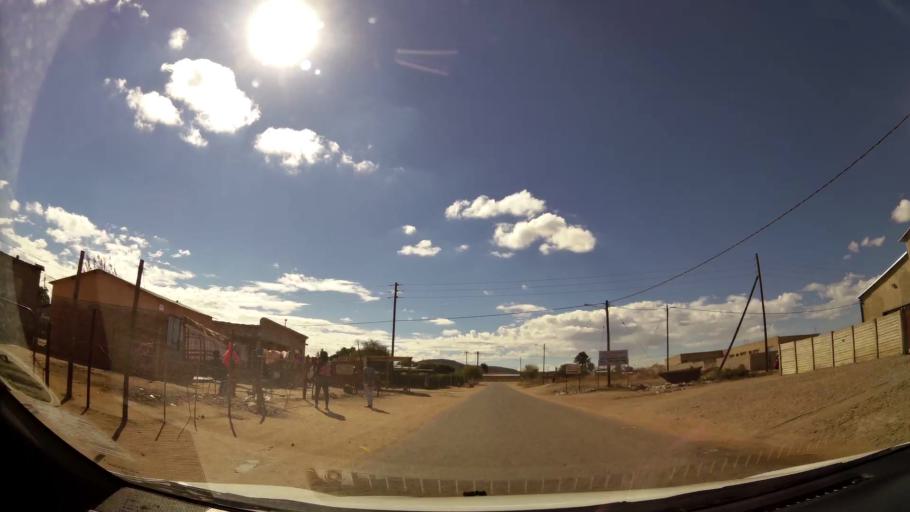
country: ZA
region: Limpopo
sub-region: Waterberg District Municipality
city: Bela-Bela
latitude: -24.8795
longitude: 28.3195
